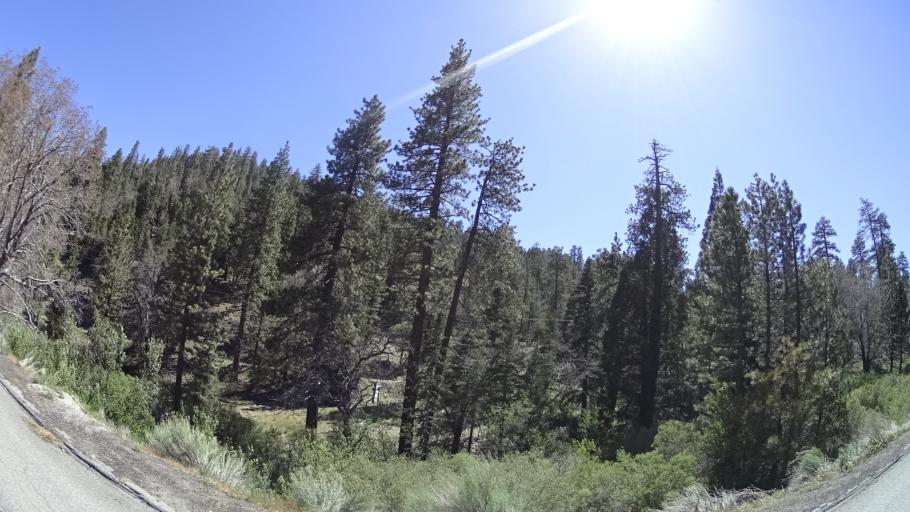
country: US
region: California
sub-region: San Bernardino County
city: Wrightwood
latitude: 34.3766
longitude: -117.6869
